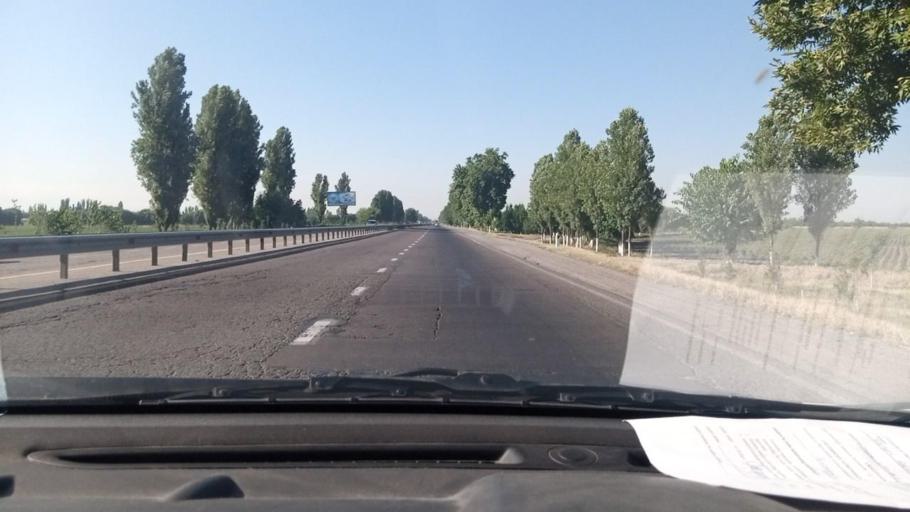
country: UZ
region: Toshkent Shahri
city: Bektemir
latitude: 41.2174
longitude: 69.4025
